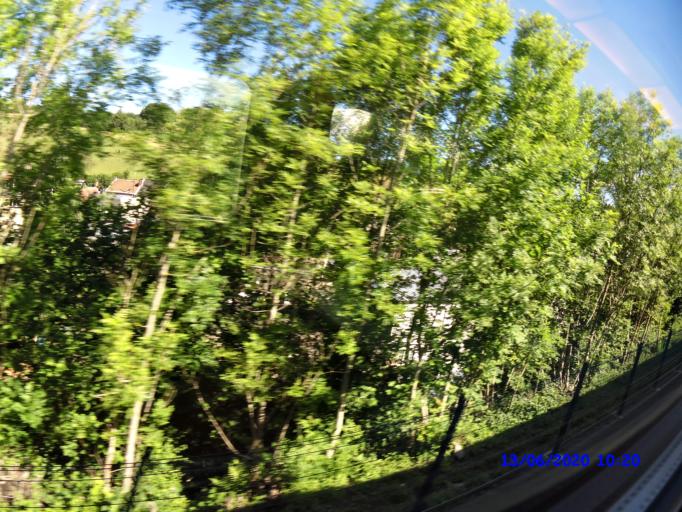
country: BE
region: Wallonia
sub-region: Province de Liege
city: Pepinster
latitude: 50.5709
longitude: 5.8263
